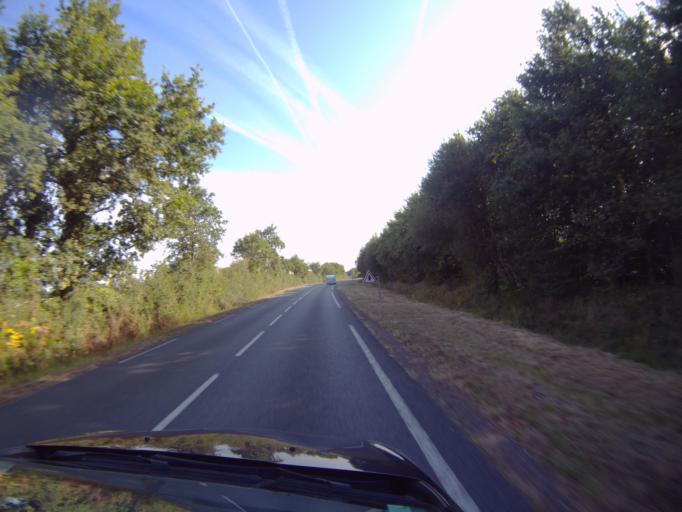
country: FR
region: Pays de la Loire
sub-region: Departement de la Vendee
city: Saint-Hilaire-de-Talmont
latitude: 46.4951
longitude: -1.5833
